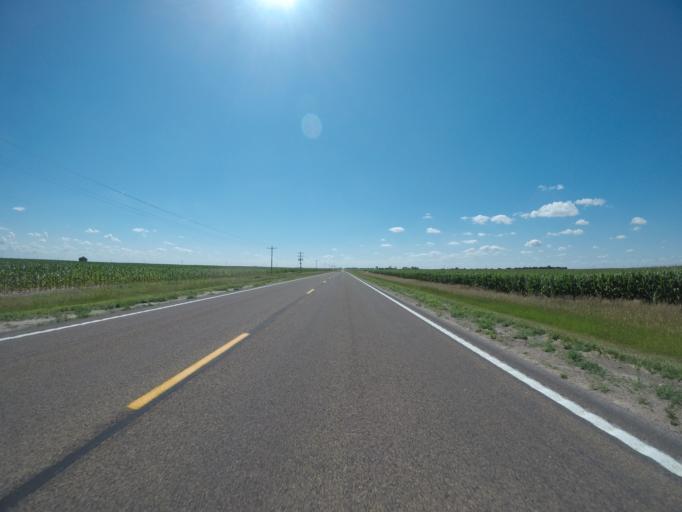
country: US
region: Nebraska
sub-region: Chase County
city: Imperial
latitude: 40.5376
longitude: -101.7352
